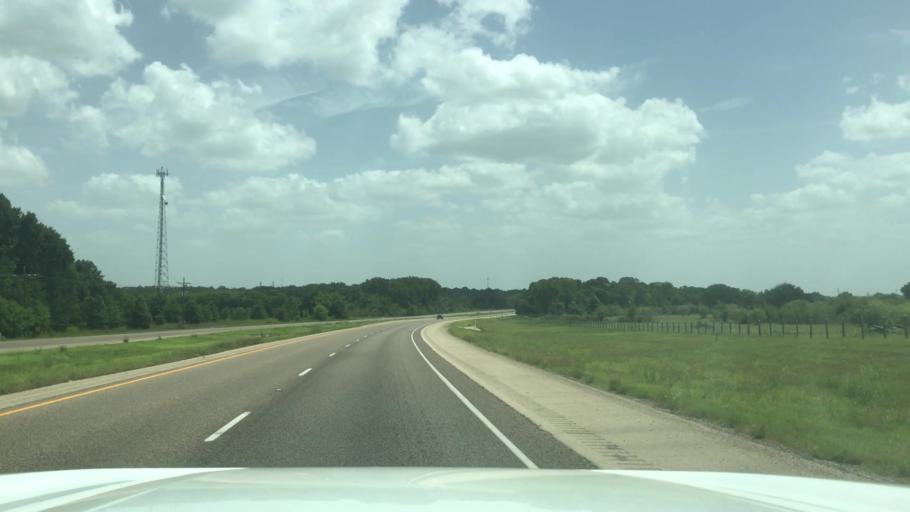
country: US
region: Texas
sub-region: Robertson County
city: Calvert
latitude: 31.1231
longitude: -96.7128
